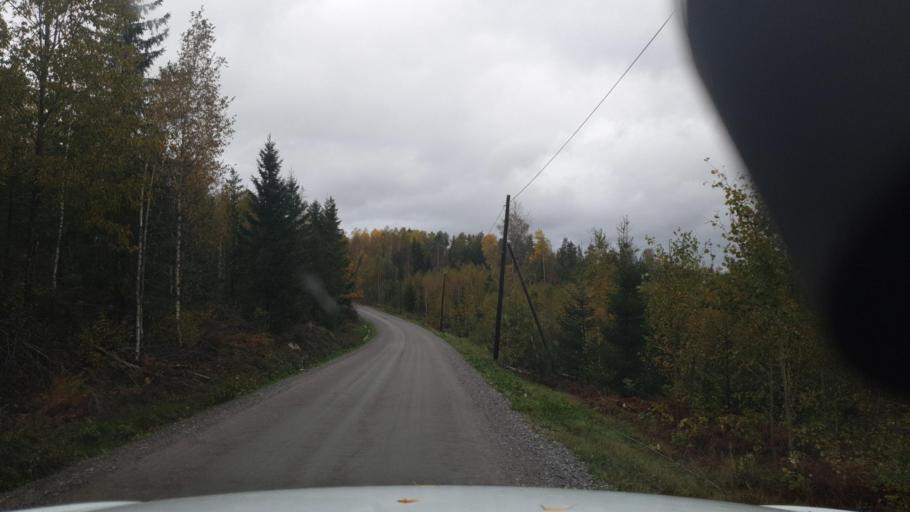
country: SE
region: Vaermland
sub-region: Karlstads Kommun
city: Edsvalla
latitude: 59.5094
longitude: 13.2076
